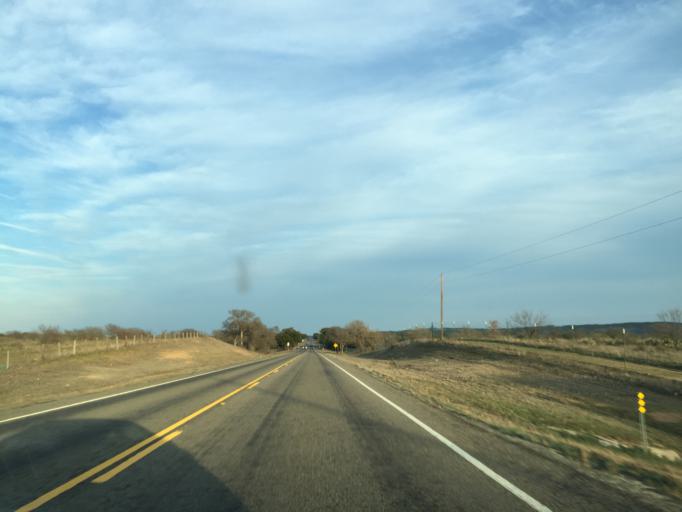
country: US
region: Texas
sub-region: Llano County
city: Buchanan Dam
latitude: 30.7328
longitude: -98.4908
